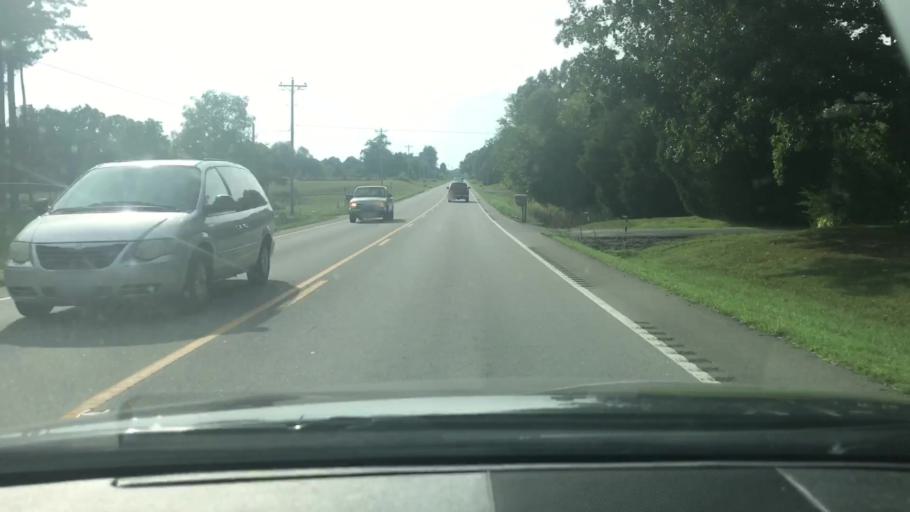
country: US
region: Tennessee
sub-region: Dickson County
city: White Bluff
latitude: 36.0333
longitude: -87.2260
